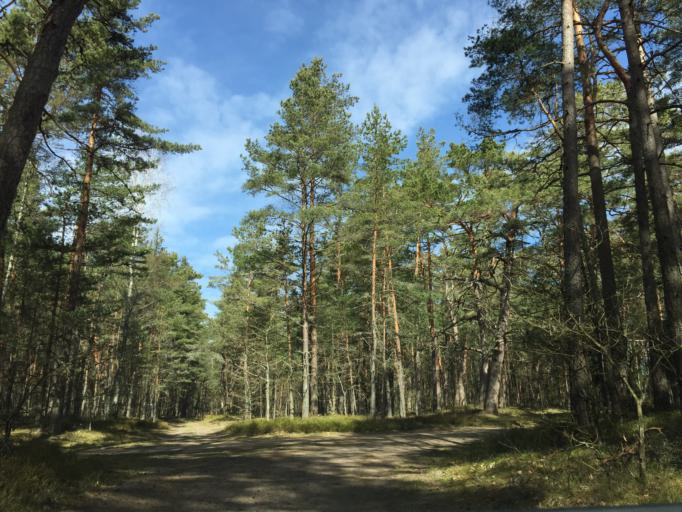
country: LV
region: Salacgrivas
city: Salacgriva
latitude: 57.6968
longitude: 24.3582
